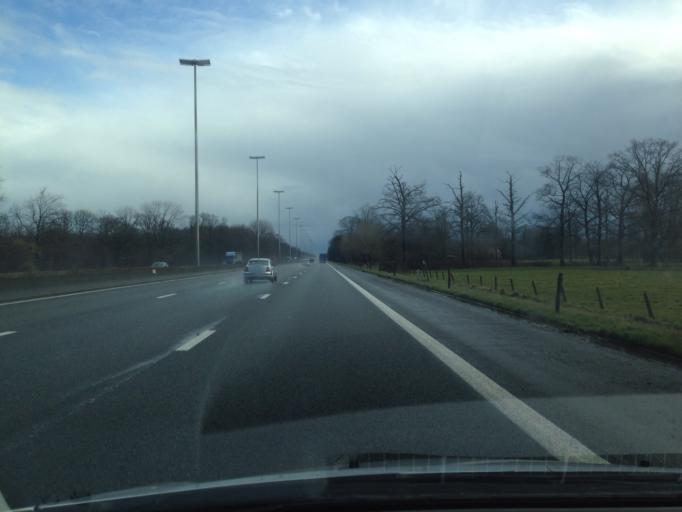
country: BE
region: Flanders
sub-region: Provincie West-Vlaanderen
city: Beernem
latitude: 51.1109
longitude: 3.3596
